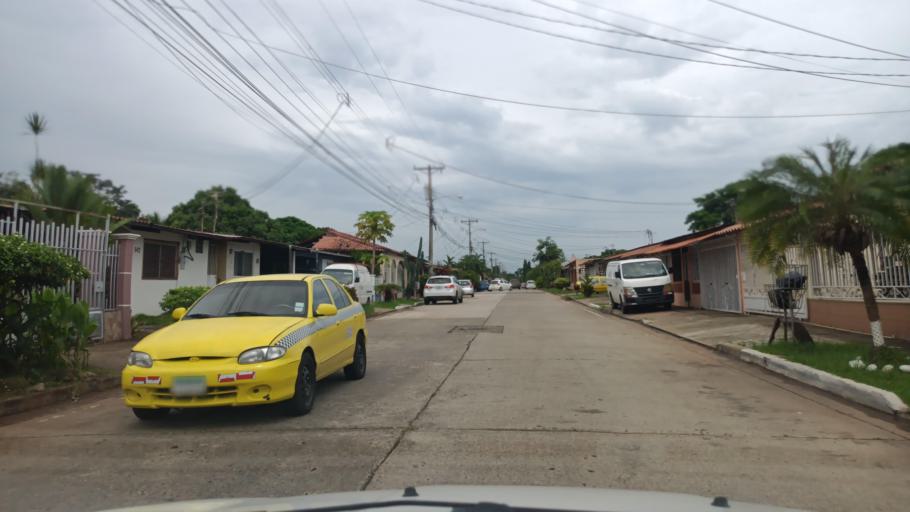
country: PA
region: Panama
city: Tocumen
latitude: 9.0488
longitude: -79.4170
